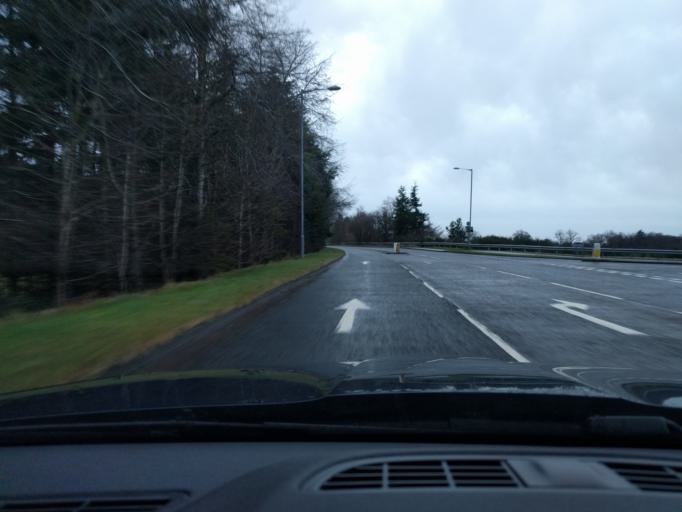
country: GB
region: Scotland
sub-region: Falkirk
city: Falkirk
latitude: 55.9889
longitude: -3.7552
